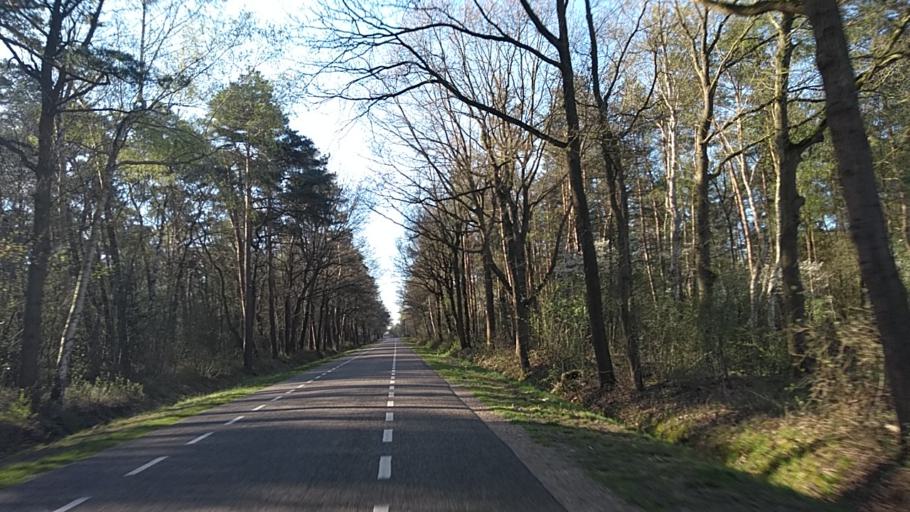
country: NL
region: Overijssel
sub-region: Gemeente Hof van Twente
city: Delden
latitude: 52.2715
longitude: 6.6701
